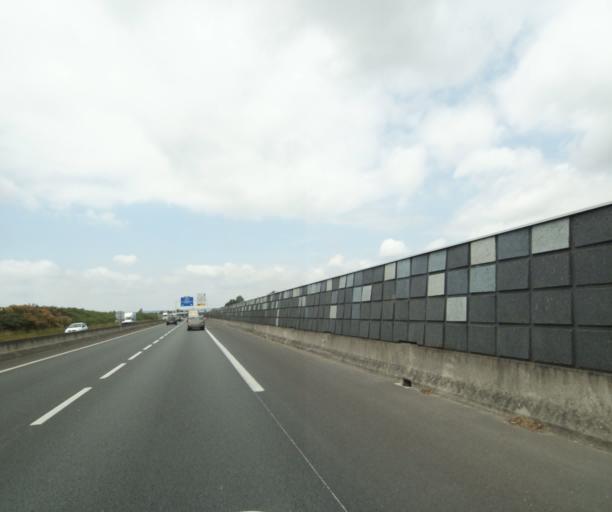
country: FR
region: Midi-Pyrenees
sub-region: Departement du Tarn-et-Garonne
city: Montauban
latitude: 44.0274
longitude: 1.3877
